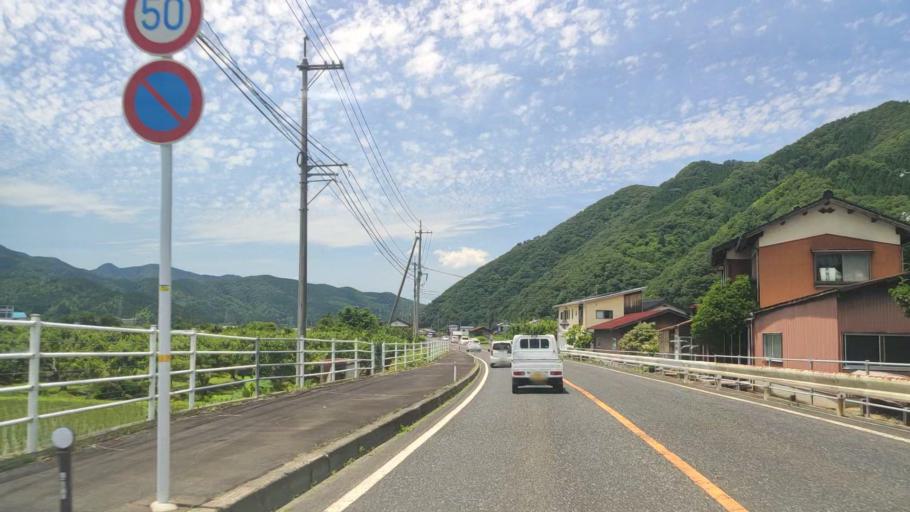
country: JP
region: Tottori
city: Tottori
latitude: 35.3664
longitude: 134.3386
